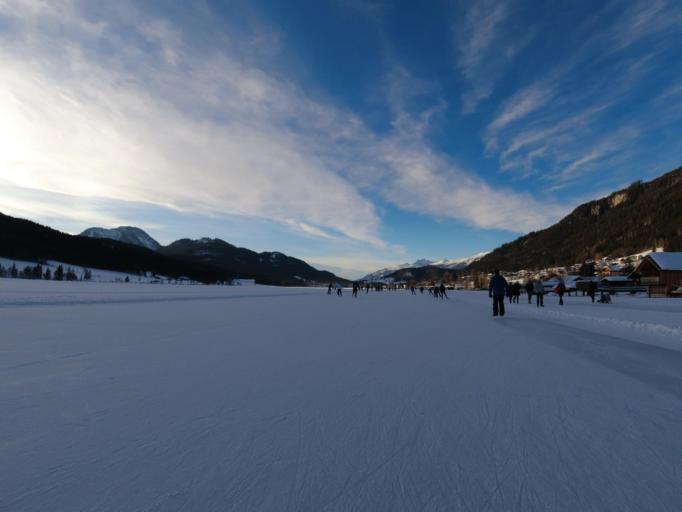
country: AT
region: Carinthia
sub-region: Politischer Bezirk Spittal an der Drau
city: Steinfeld
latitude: 46.7172
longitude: 13.2831
